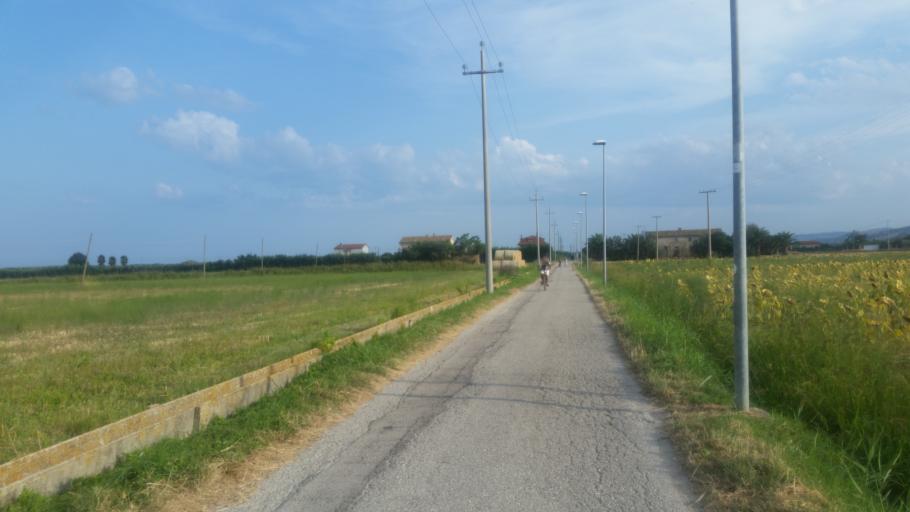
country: IT
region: The Marches
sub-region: Provincia di Ascoli Piceno
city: San Benedetto del Tronto
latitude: 42.9082
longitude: 13.9015
